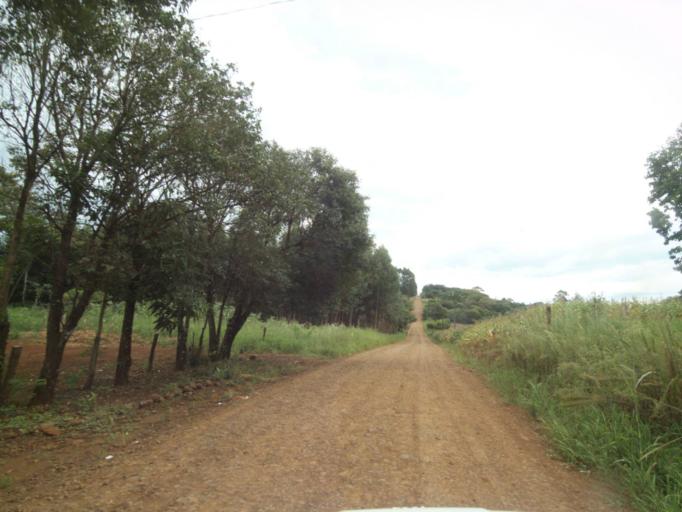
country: BR
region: Parana
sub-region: Guaraniacu
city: Guaraniacu
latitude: -24.9104
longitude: -52.9357
